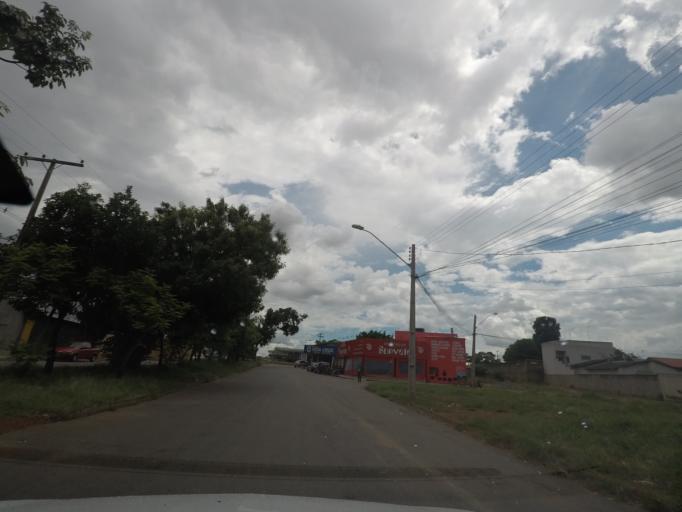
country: BR
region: Goias
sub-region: Goiania
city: Goiania
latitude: -16.7360
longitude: -49.3434
